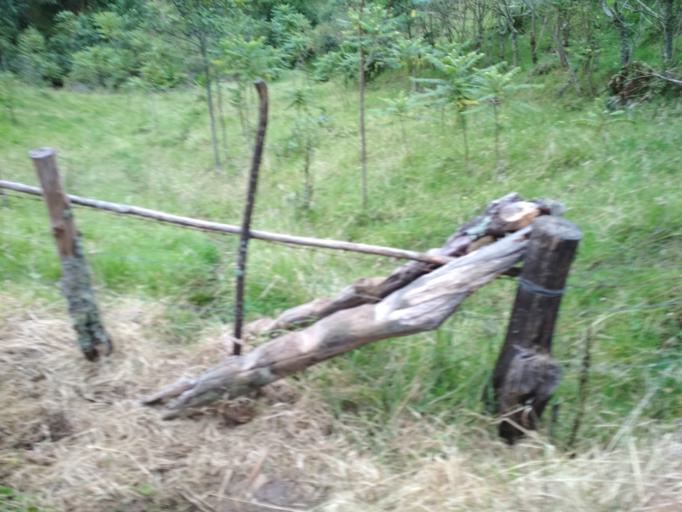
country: CO
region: Cauca
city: Jambalo
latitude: 2.7387
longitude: -76.3463
